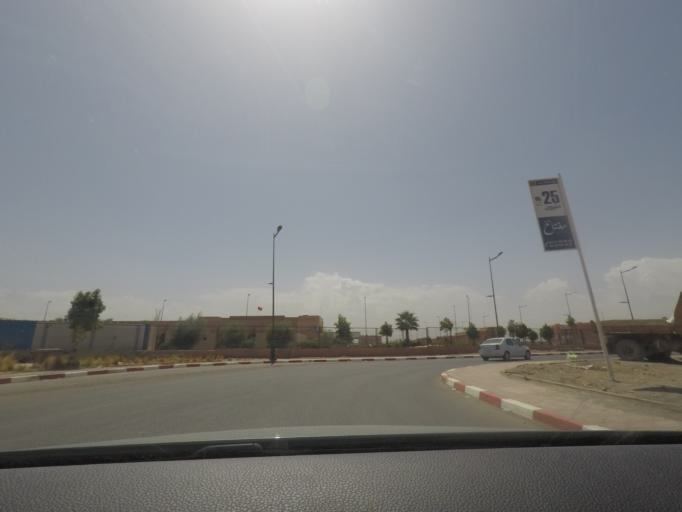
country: MA
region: Marrakech-Tensift-Al Haouz
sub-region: Marrakech
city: Marrakesh
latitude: 31.5913
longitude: -8.0317
